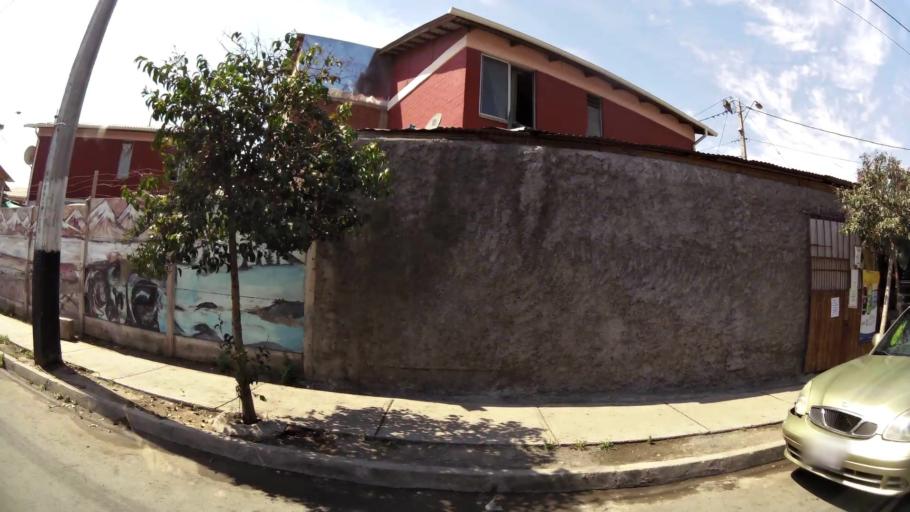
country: CL
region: Santiago Metropolitan
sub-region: Provincia de Santiago
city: La Pintana
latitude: -33.5898
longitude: -70.6099
